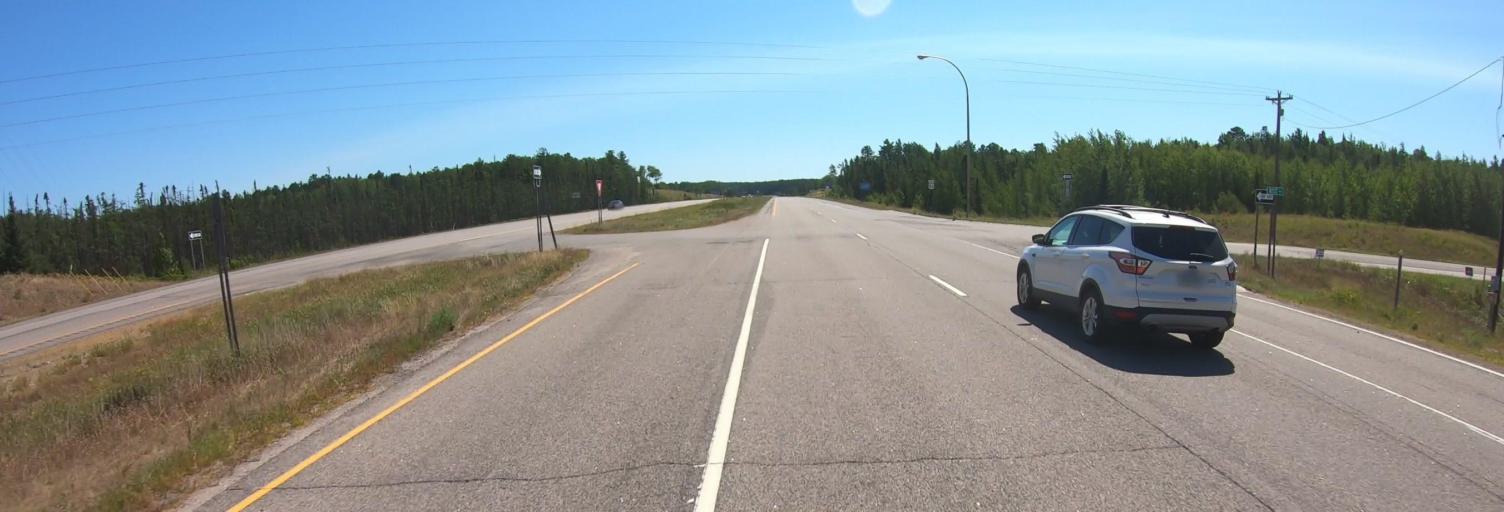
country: US
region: Minnesota
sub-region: Saint Louis County
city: Mountain Iron
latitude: 47.6645
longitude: -92.6349
